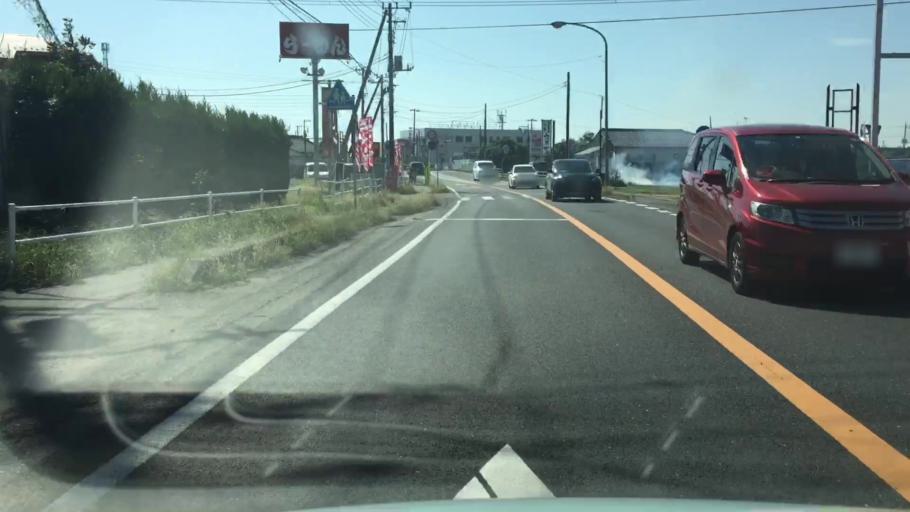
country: JP
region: Ibaraki
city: Ryugasaki
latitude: 35.8682
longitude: 140.1537
